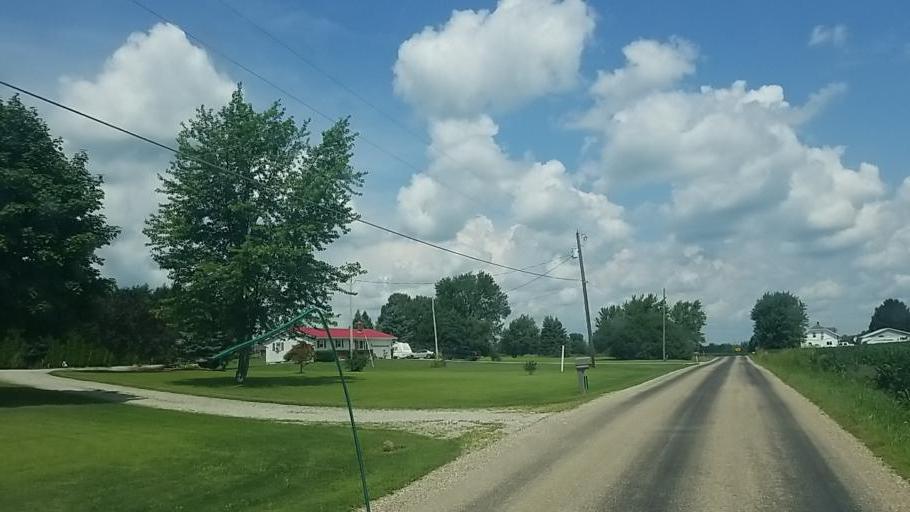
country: US
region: Ohio
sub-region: Wayne County
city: West Salem
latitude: 40.9892
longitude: -82.0788
